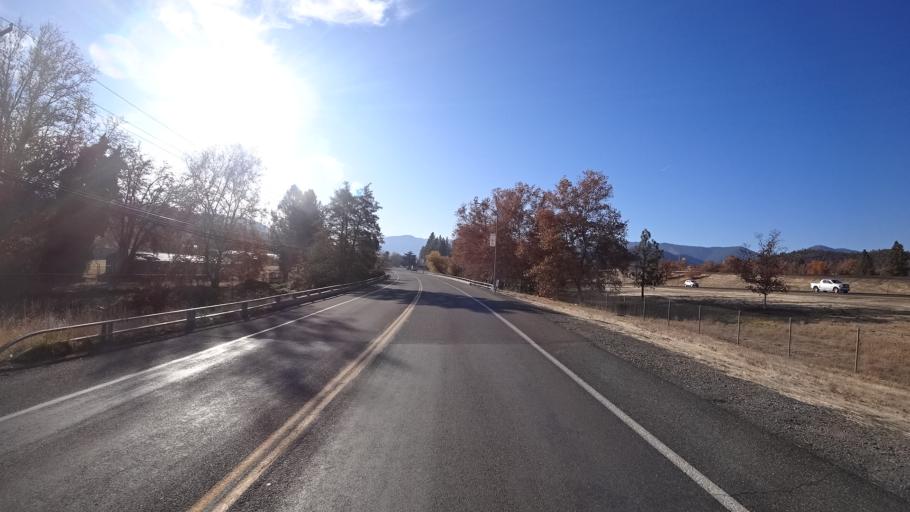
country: US
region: California
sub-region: Siskiyou County
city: Yreka
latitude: 41.7063
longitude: -122.6420
